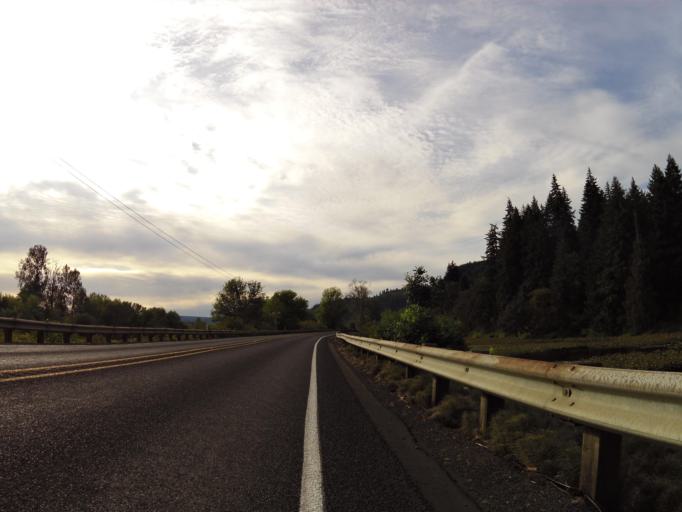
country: US
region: Washington
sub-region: Cowlitz County
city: West Longview
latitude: 46.1833
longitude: -123.0757
